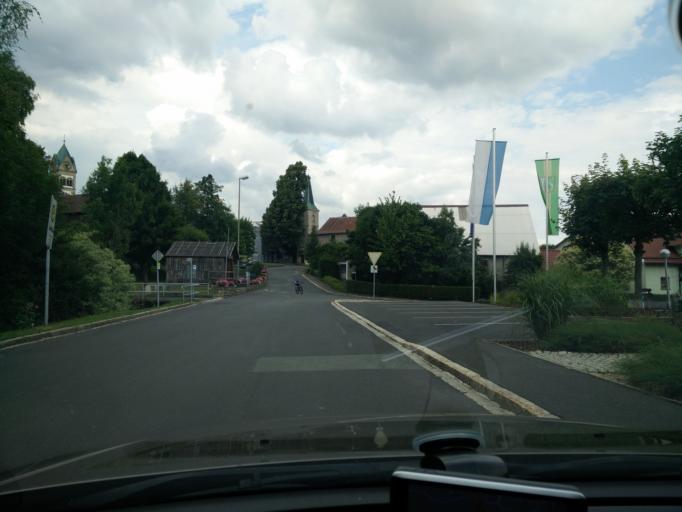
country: DE
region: Bavaria
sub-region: Upper Franconia
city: Mehlmeisel
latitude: 49.9757
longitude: 11.8549
